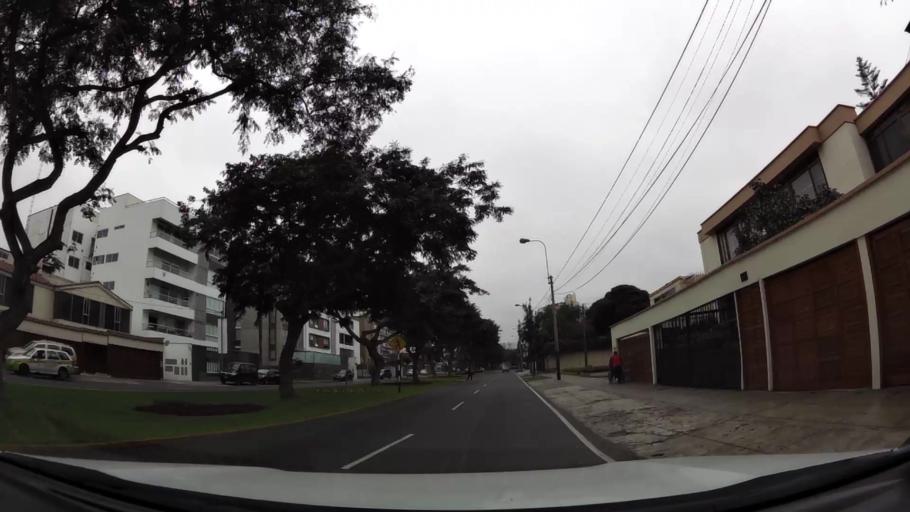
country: PE
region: Lima
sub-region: Lima
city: Surco
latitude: -12.1204
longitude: -77.0127
